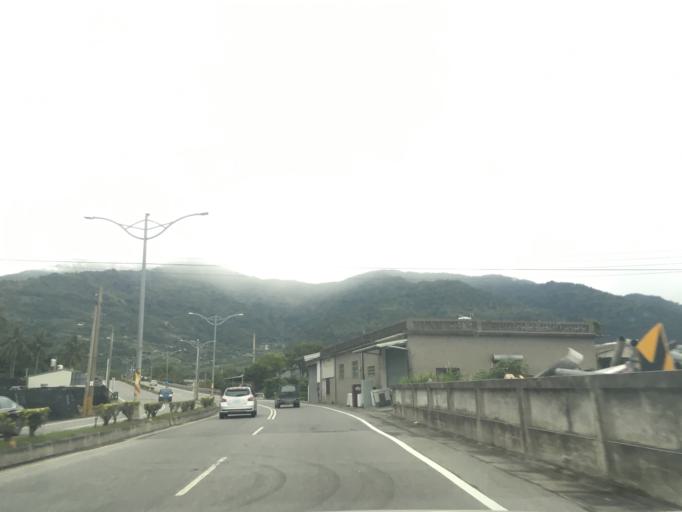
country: TW
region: Taiwan
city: Taitung City
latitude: 22.6985
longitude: 121.0423
